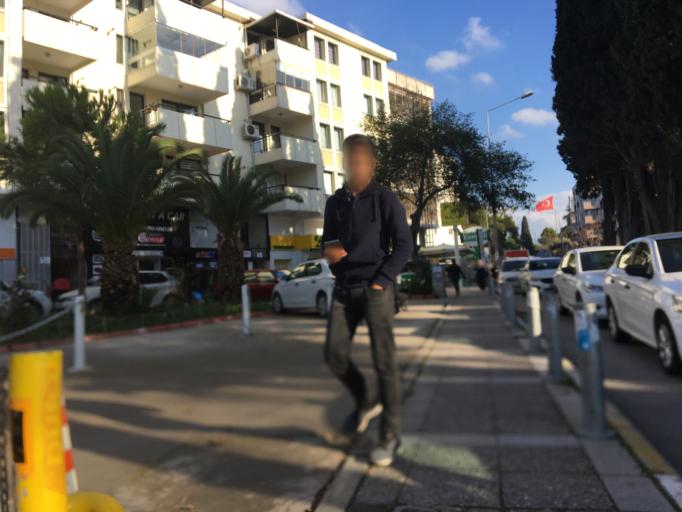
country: TR
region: Izmir
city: Buca
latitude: 38.3892
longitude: 27.1694
